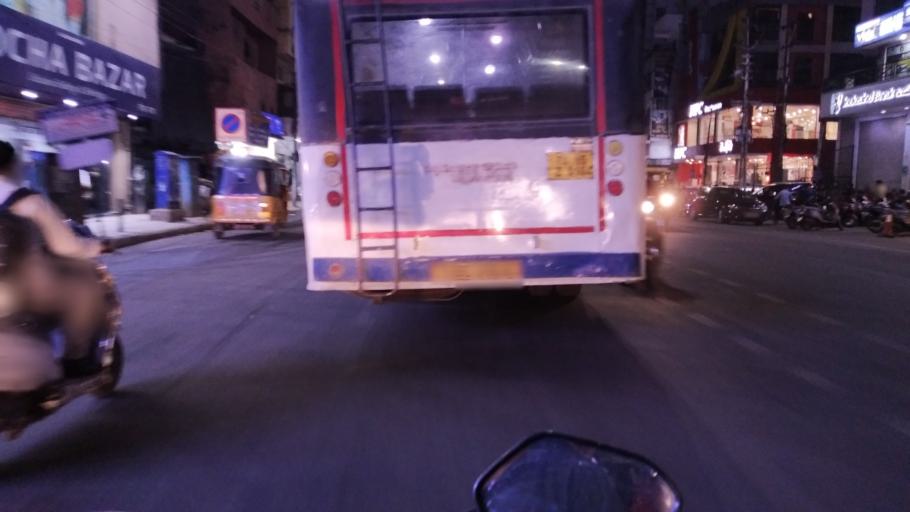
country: IN
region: Telangana
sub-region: Hyderabad
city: Malkajgiri
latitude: 17.4365
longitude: 78.4886
